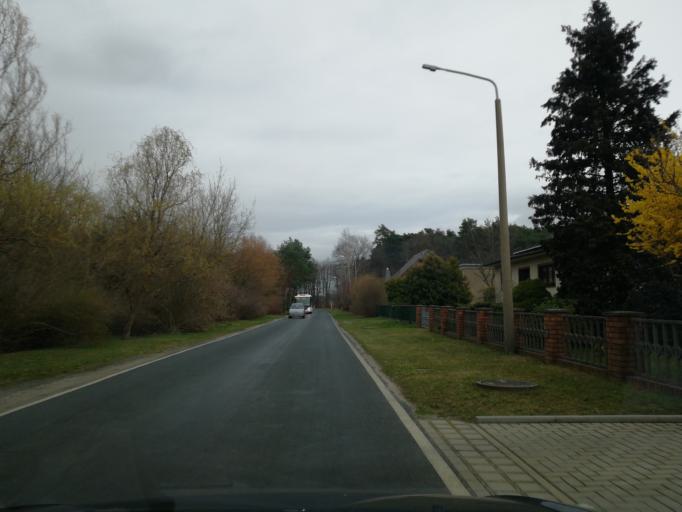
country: DE
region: Brandenburg
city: Calau
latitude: 51.7437
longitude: 13.9842
